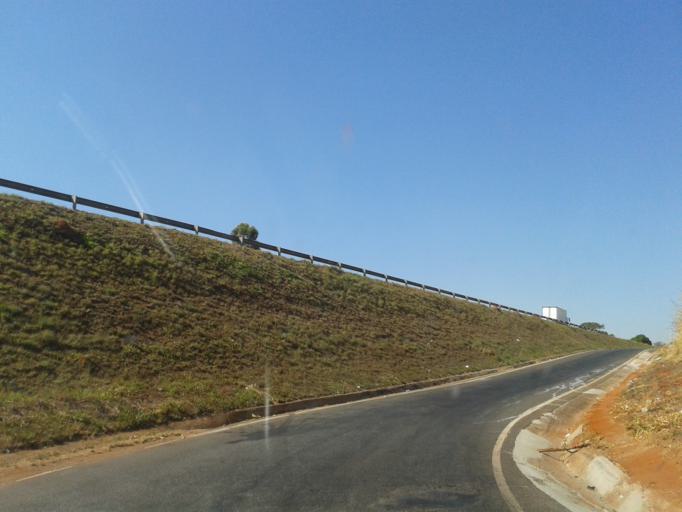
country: BR
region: Goias
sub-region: Hidrolandia
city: Hidrolandia
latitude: -17.1768
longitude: -49.2106
